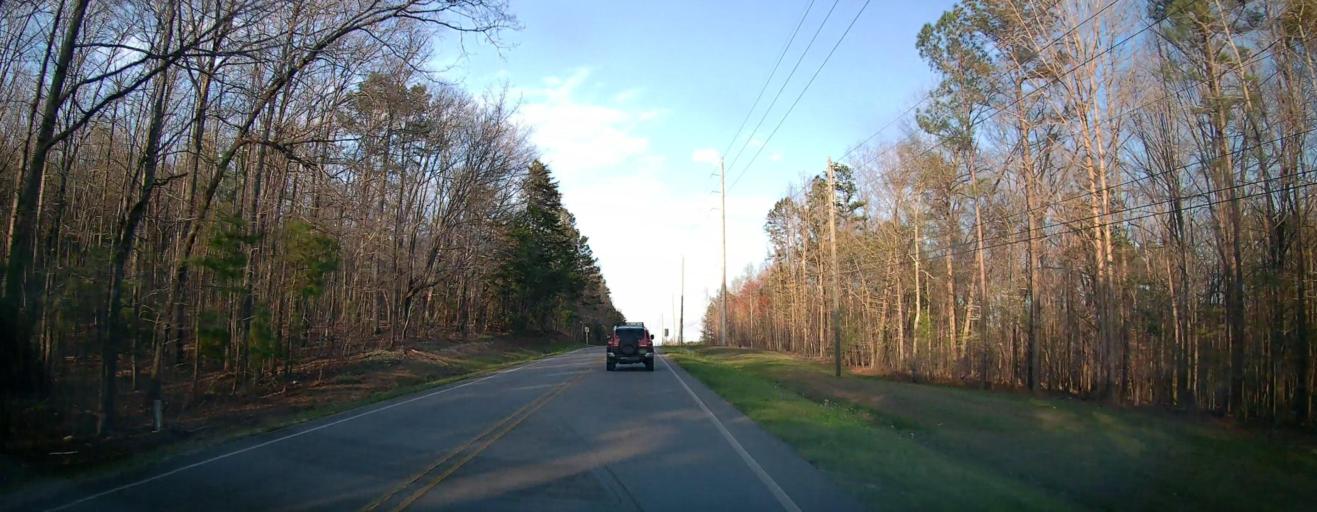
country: US
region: Alabama
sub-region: Shelby County
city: Chelsea
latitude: 33.3339
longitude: -86.6856
